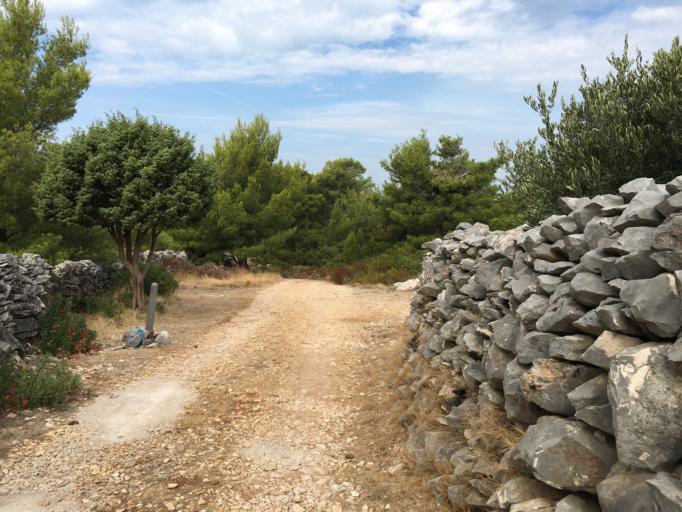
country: HR
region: Splitsko-Dalmatinska
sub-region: Grad Hvar
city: Hvar
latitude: 43.1643
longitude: 16.4463
